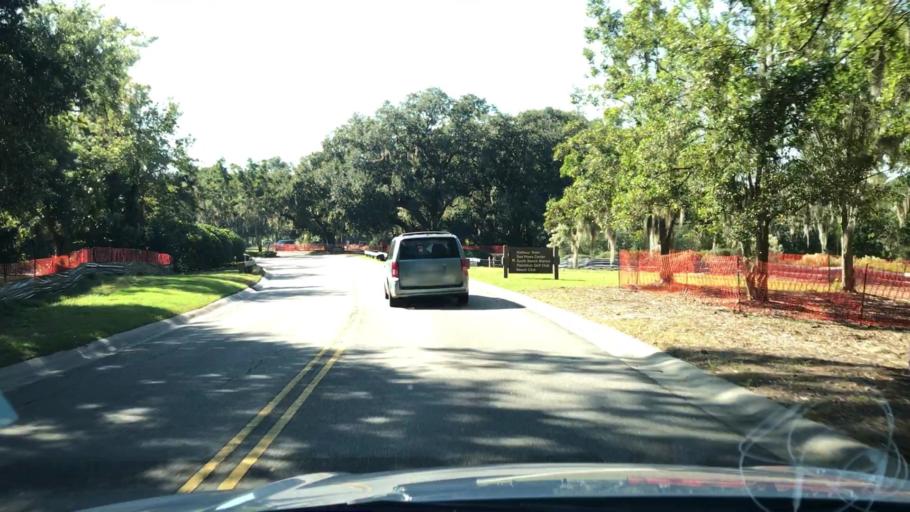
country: US
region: South Carolina
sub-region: Beaufort County
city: Hilton Head Island
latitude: 32.1444
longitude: -80.7884
